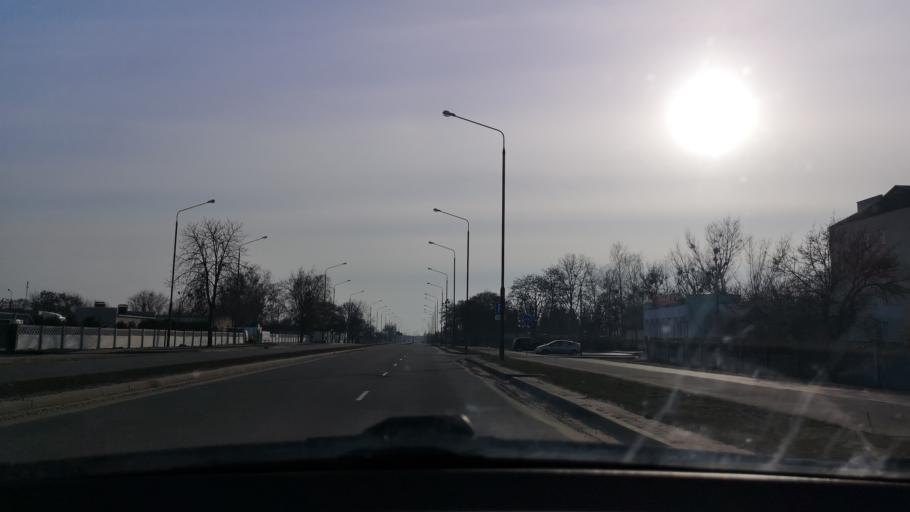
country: BY
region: Brest
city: Brest
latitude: 52.1199
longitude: 23.6705
